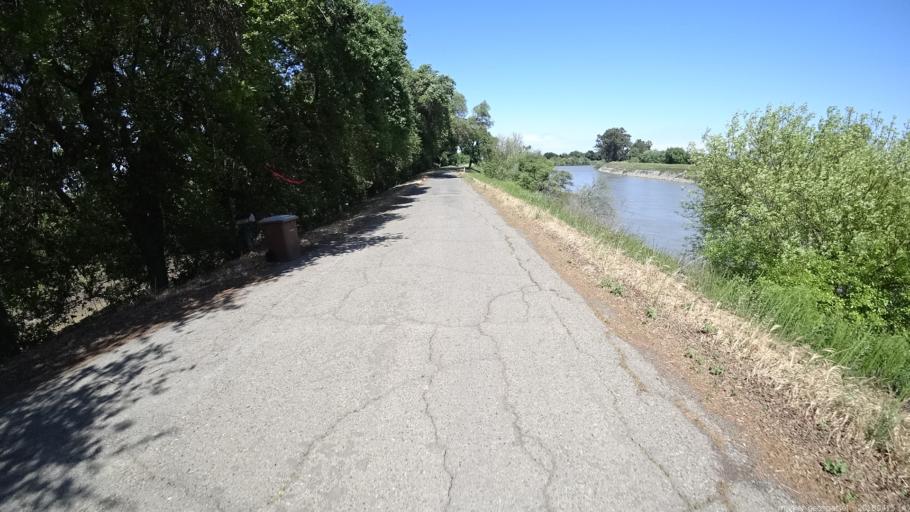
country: US
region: California
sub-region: Sacramento County
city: Walnut Grove
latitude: 38.2804
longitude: -121.5897
